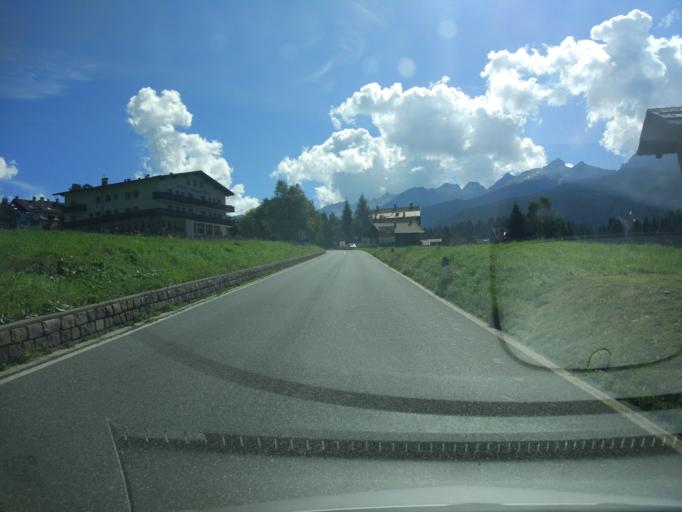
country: IT
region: Trentino-Alto Adige
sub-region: Provincia di Trento
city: Predazzo
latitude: 46.3147
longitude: 11.6586
